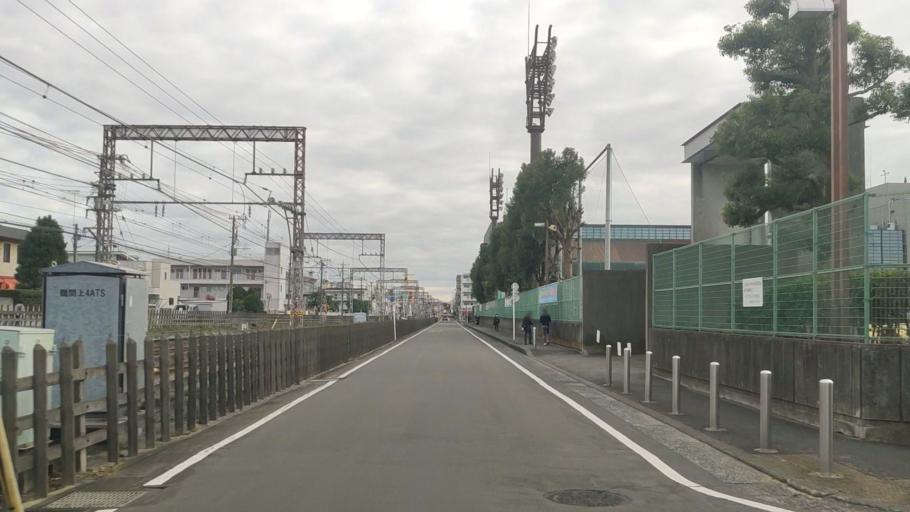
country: JP
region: Kanagawa
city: Minami-rinkan
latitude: 35.4766
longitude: 139.4578
